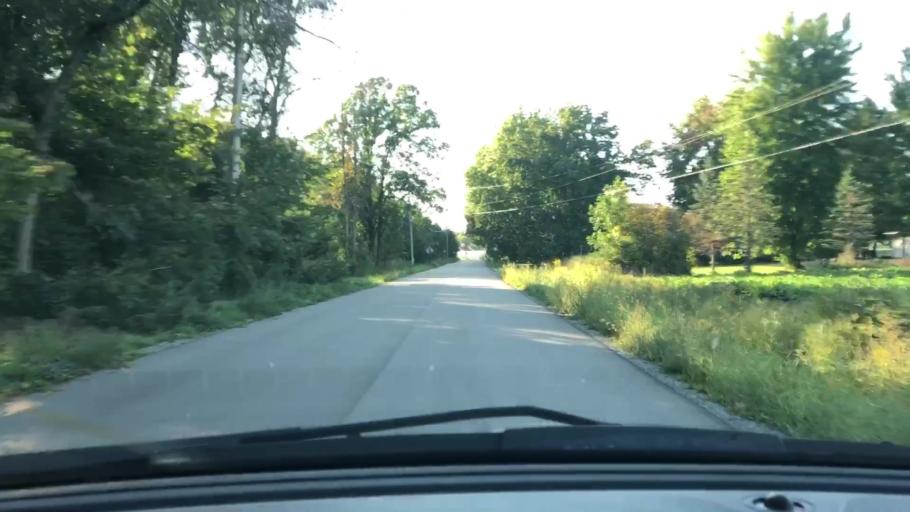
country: US
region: Michigan
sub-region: Bay County
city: Auburn
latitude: 43.6318
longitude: -84.0450
